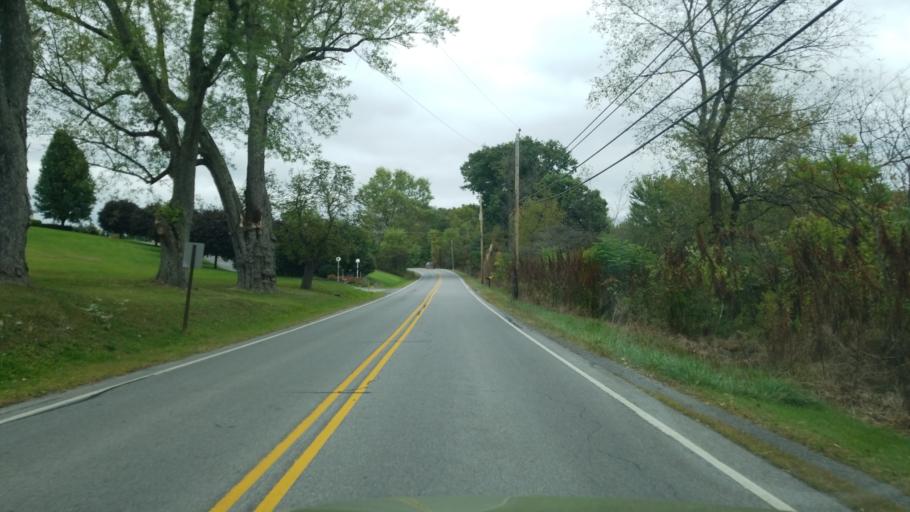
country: US
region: Pennsylvania
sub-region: Clearfield County
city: Hyde
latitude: 40.9927
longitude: -78.4692
